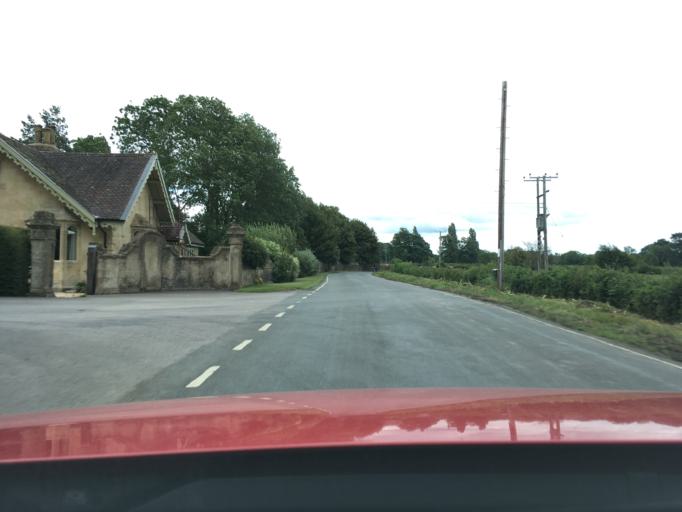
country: GB
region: England
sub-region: Gloucestershire
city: Dursley
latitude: 51.7792
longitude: -2.3825
